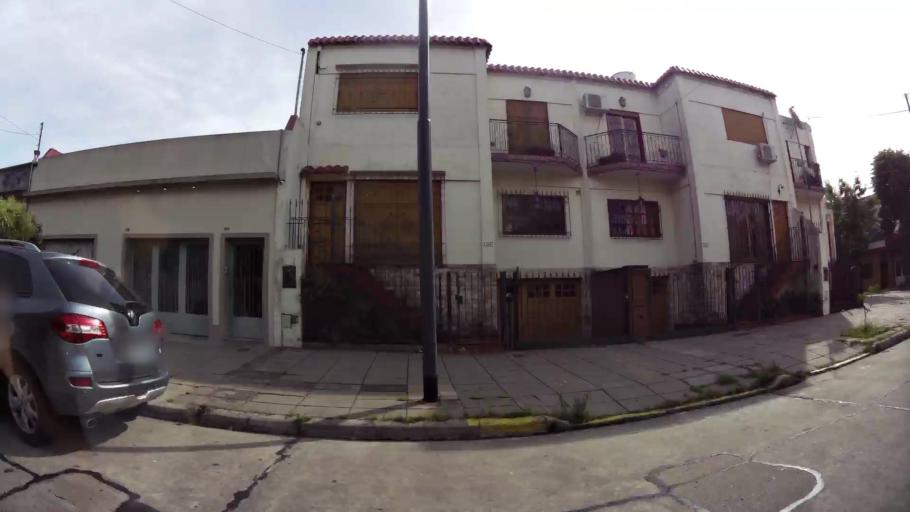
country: AR
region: Buenos Aires F.D.
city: Villa Lugano
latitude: -34.6512
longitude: -58.4805
